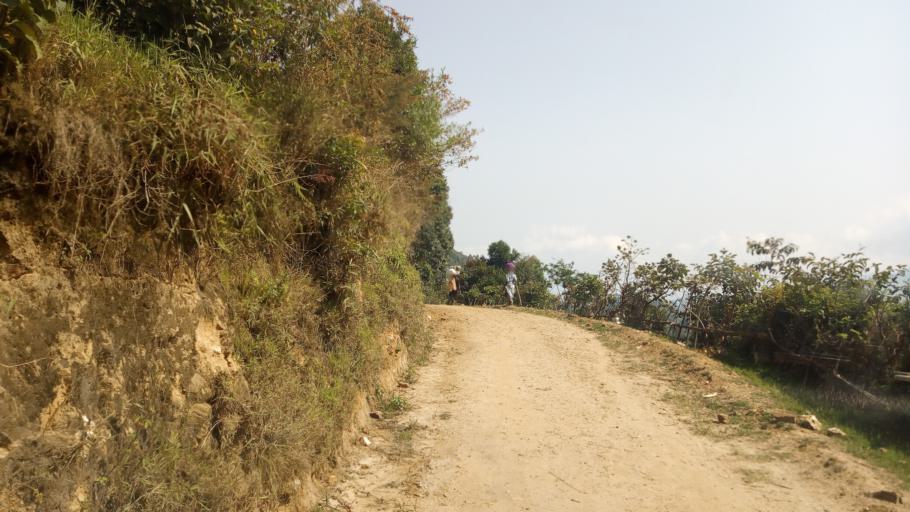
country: UG
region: Western Region
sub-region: Kisoro District
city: Kisoro
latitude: -1.1131
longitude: 29.5947
